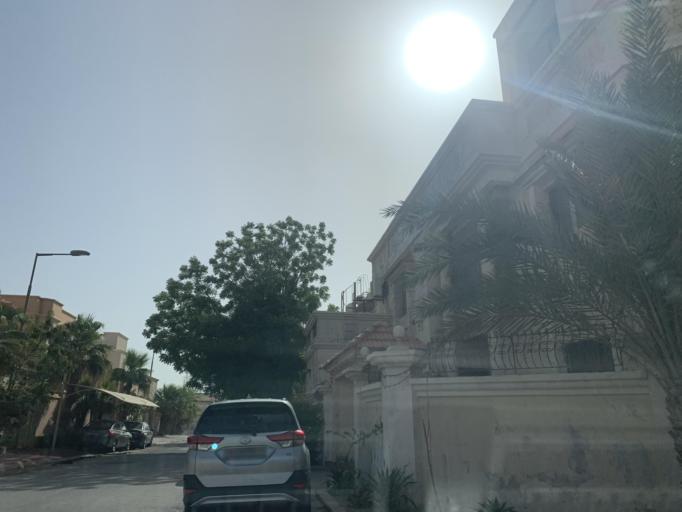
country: BH
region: Northern
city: Ar Rifa'
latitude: 26.1452
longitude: 50.5787
